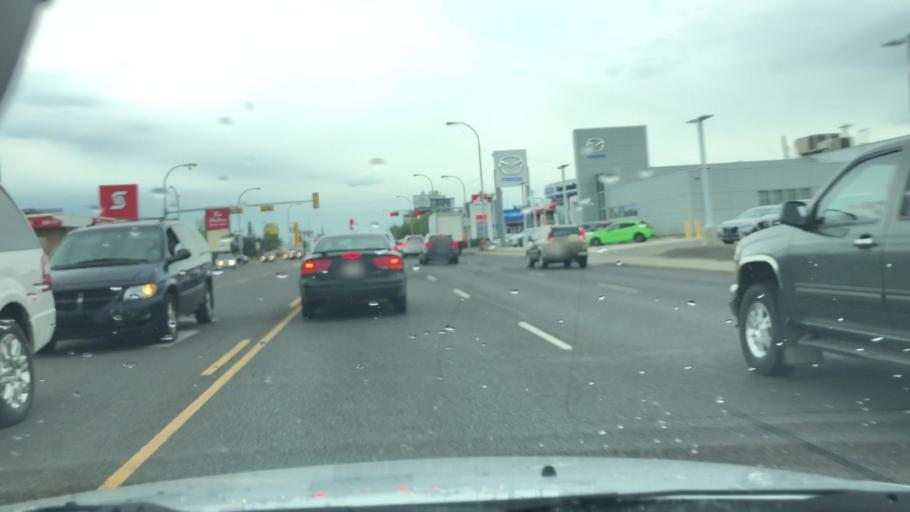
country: CA
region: Alberta
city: Edmonton
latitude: 53.5911
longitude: -113.4920
